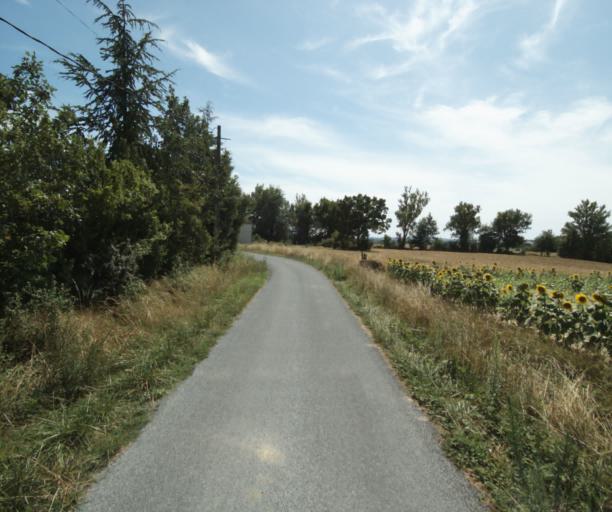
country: FR
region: Midi-Pyrenees
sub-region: Departement du Tarn
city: Puylaurens
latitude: 43.5346
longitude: 2.0026
